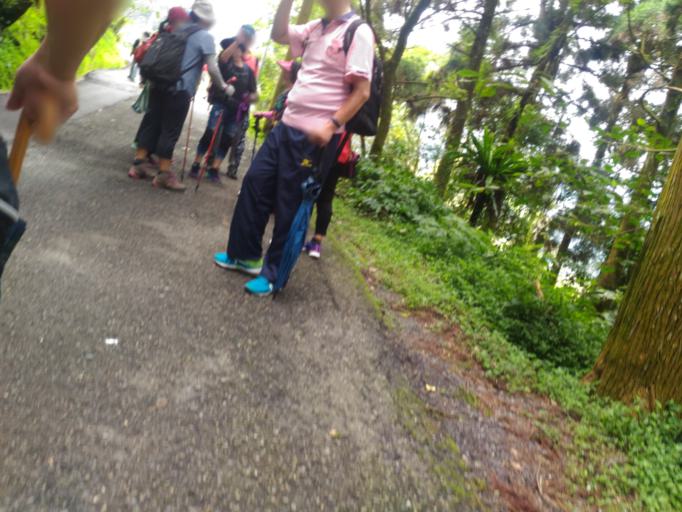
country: TW
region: Taiwan
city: Lugu
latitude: 23.6666
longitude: 120.8004
